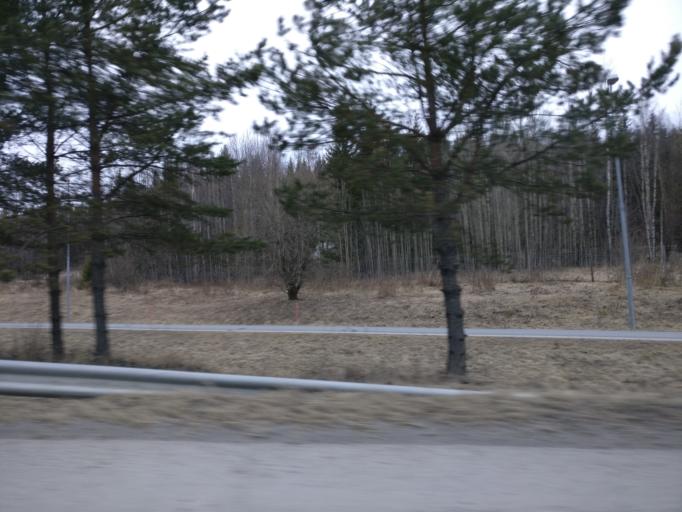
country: FI
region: Pirkanmaa
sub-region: Tampere
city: Tampere
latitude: 61.4630
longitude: 23.7736
